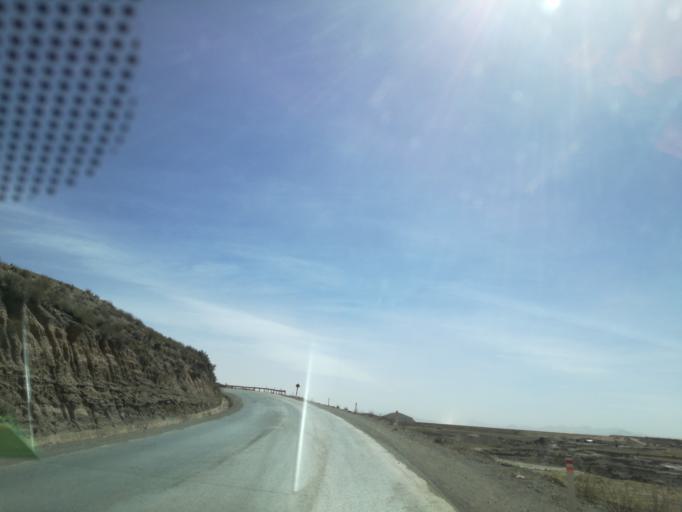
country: BO
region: Oruro
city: Oruro
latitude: -17.8219
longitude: -67.0264
